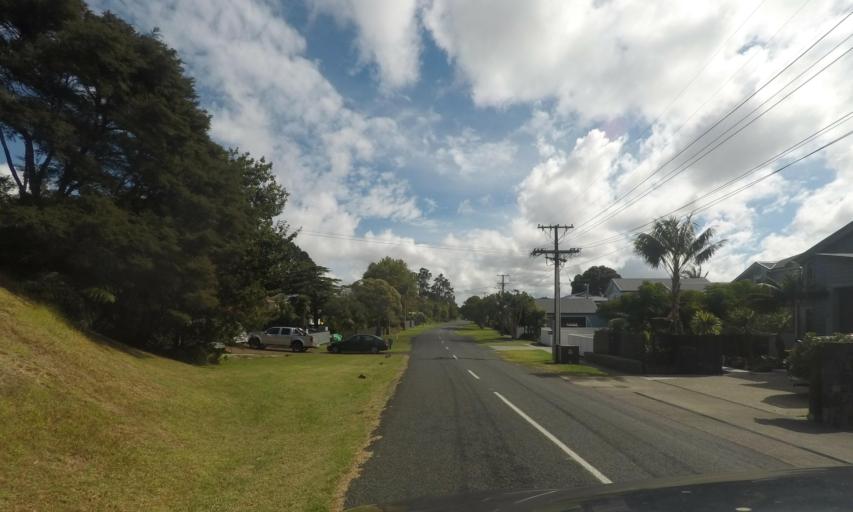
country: NZ
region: Auckland
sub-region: Auckland
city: North Shore
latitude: -36.7780
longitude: 174.6580
